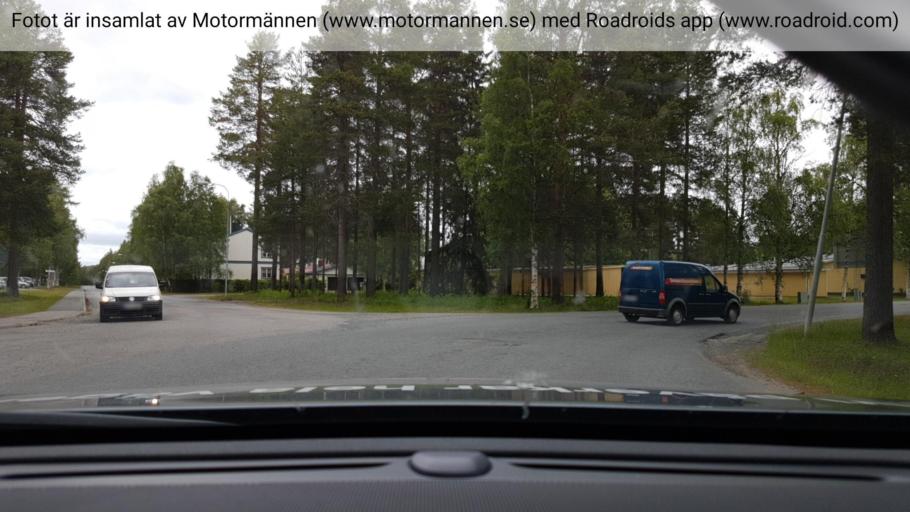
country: SE
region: Vaesterbotten
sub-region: Sorsele Kommun
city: Sorsele
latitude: 65.5370
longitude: 17.5428
